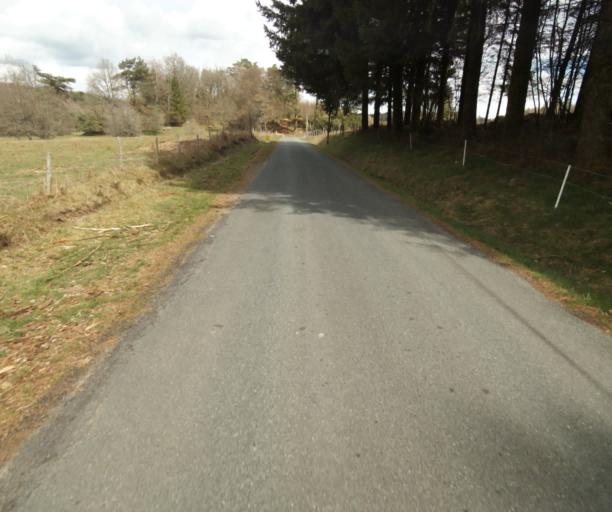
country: FR
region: Limousin
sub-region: Departement de la Correze
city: Correze
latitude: 45.3822
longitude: 1.9548
